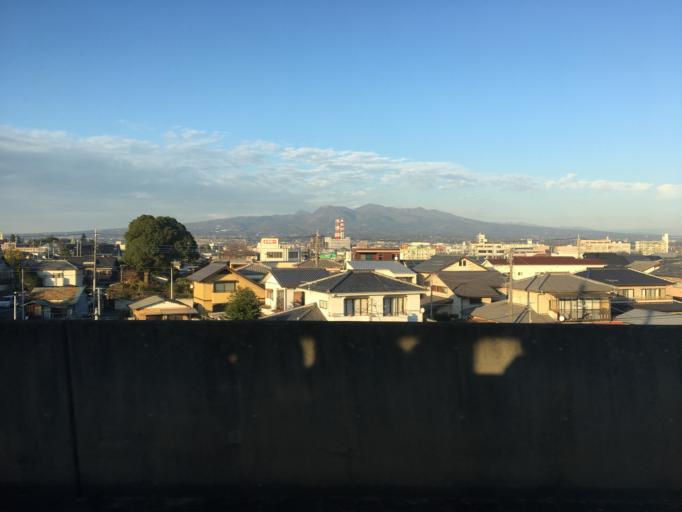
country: JP
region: Gunma
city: Maebashi-shi
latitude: 36.3829
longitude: 139.0852
